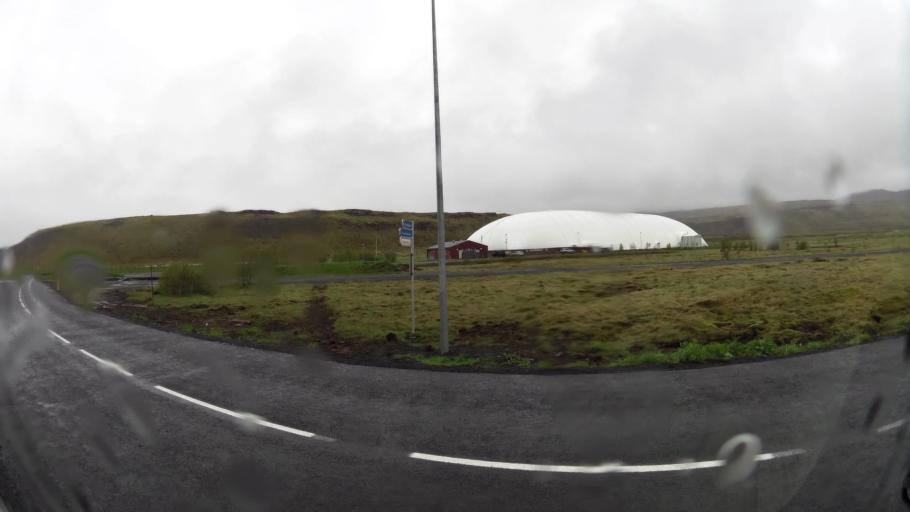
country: IS
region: South
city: Hveragerdi
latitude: 64.0117
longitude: -21.1916
